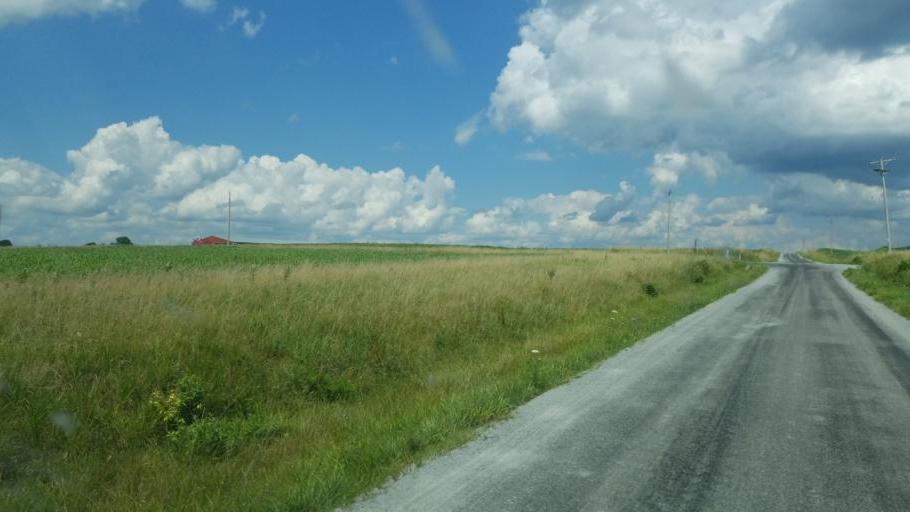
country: US
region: Ohio
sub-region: Highland County
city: Greenfield
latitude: 39.2469
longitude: -83.4282
